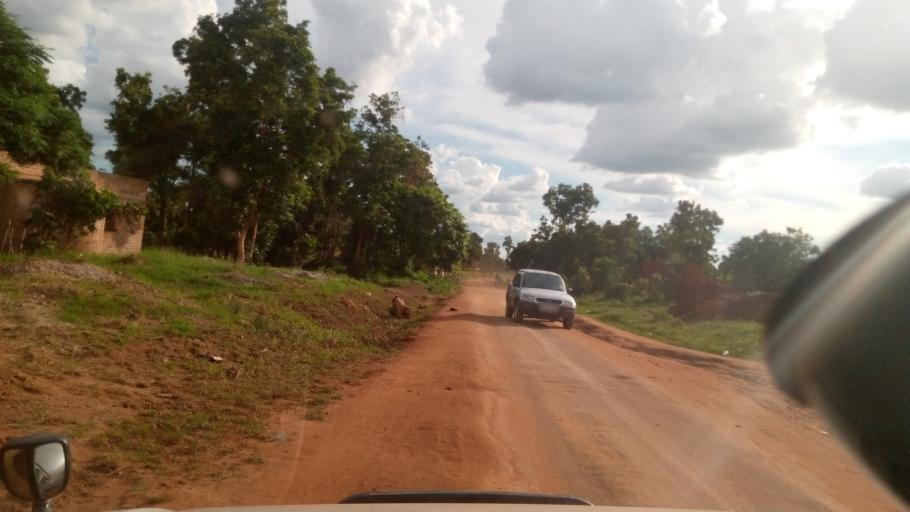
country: UG
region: Northern Region
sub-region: Lira District
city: Lira
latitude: 2.2284
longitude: 32.8993
